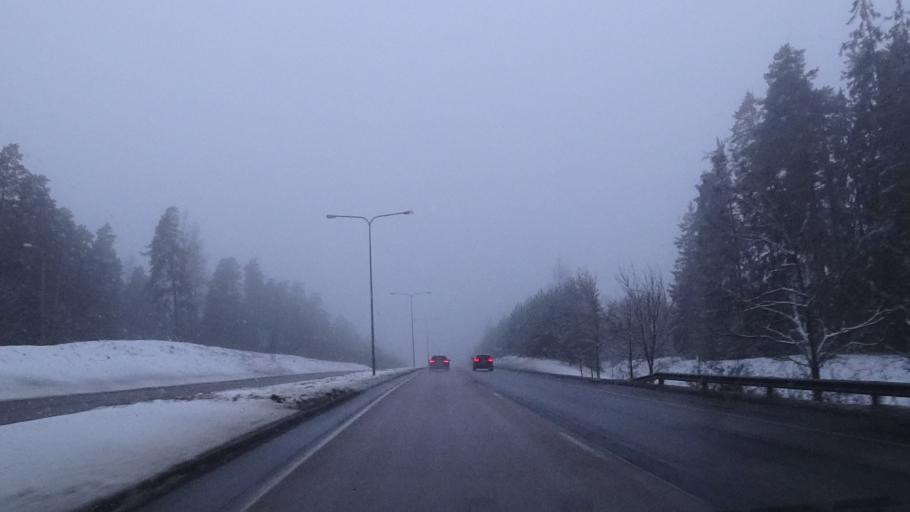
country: FI
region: Paijanne Tavastia
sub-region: Lahti
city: Hollola
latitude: 60.9868
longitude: 25.5354
